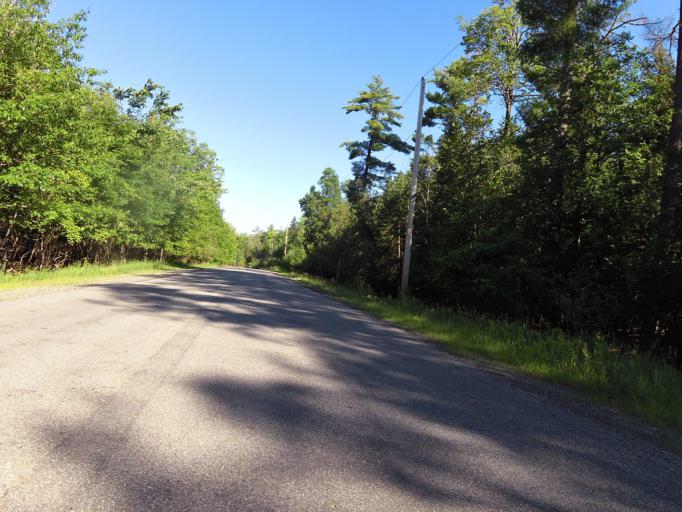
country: CA
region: Ontario
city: Arnprior
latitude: 45.4617
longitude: -76.2796
